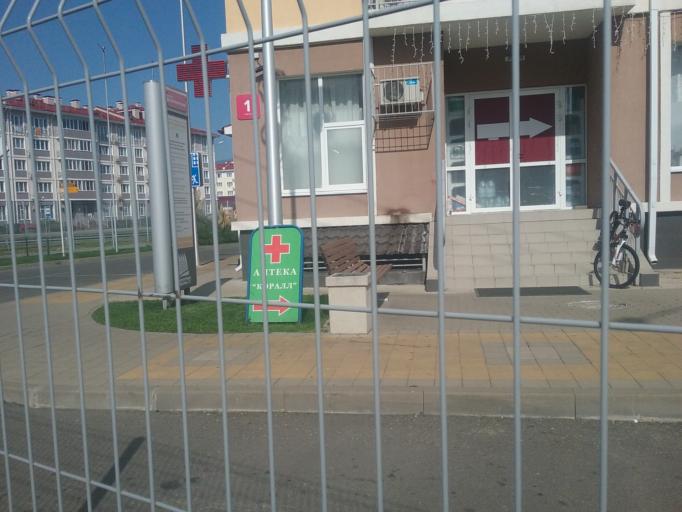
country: RU
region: Krasnodarskiy
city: Vysokoye
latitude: 43.3905
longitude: 39.9909
